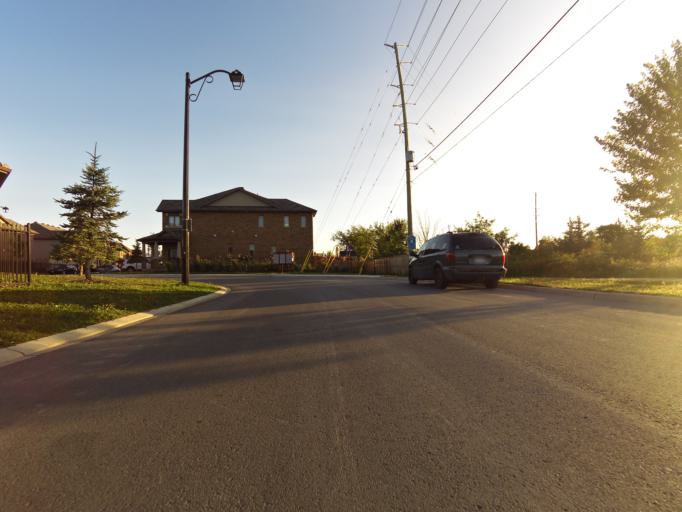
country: CA
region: Ontario
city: Bells Corners
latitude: 45.2825
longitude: -75.7486
